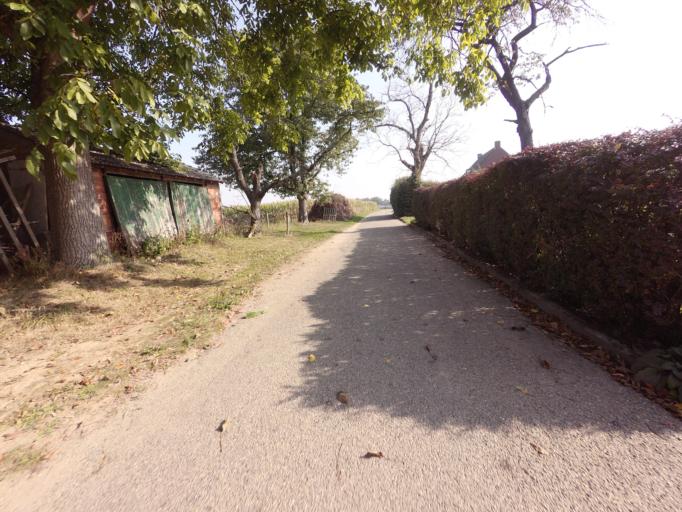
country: NL
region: Limburg
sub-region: Gemeente Beesel
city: Beesel
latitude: 51.2459
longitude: 6.0287
